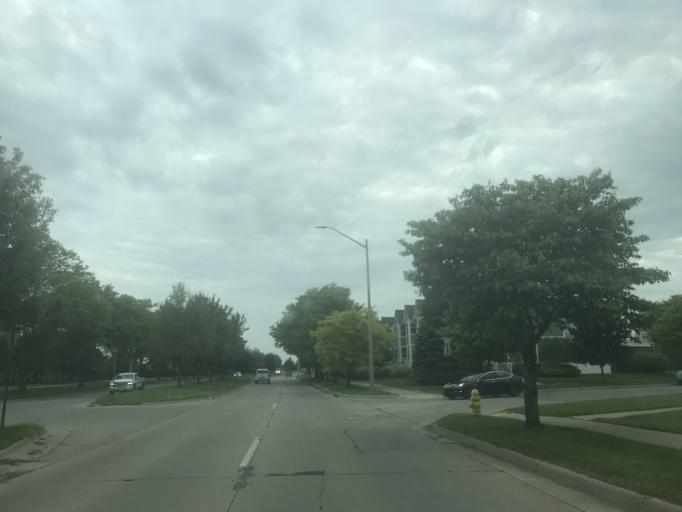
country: US
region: Michigan
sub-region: Wayne County
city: Wyandotte
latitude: 42.1950
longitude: -83.1532
